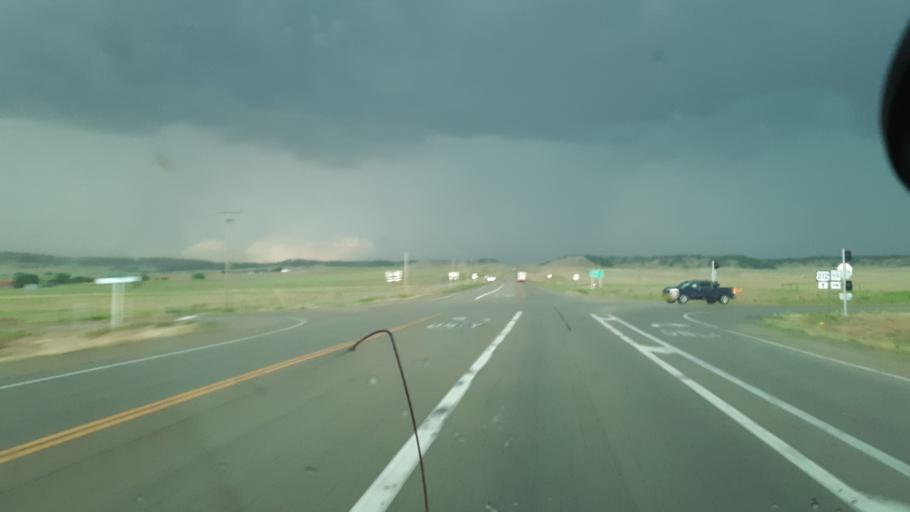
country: US
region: Montana
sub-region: Powder River County
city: Broadus
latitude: 45.4658
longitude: -105.4613
